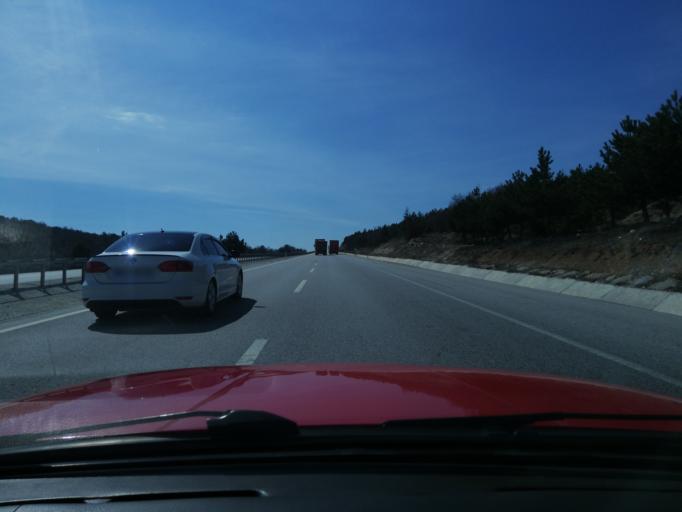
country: TR
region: Kuetahya
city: Kutahya
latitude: 39.3535
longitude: 30.0563
